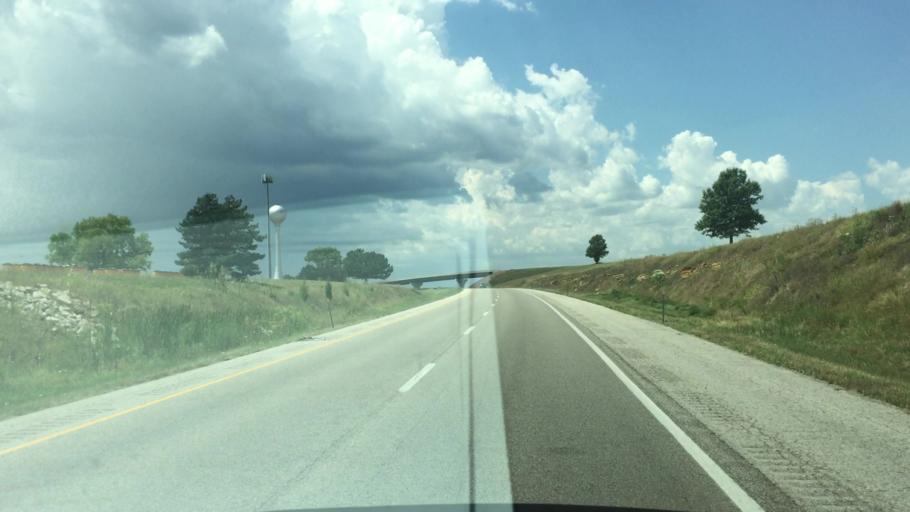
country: US
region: Kansas
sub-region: Shawnee County
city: Topeka
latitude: 39.0318
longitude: -95.6028
